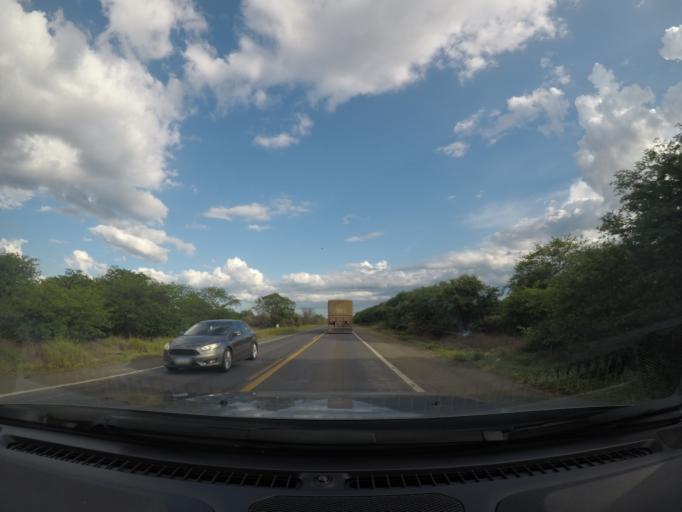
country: BR
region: Bahia
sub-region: Oliveira Dos Brejinhos
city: Beira Rio
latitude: -12.1822
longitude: -42.8327
